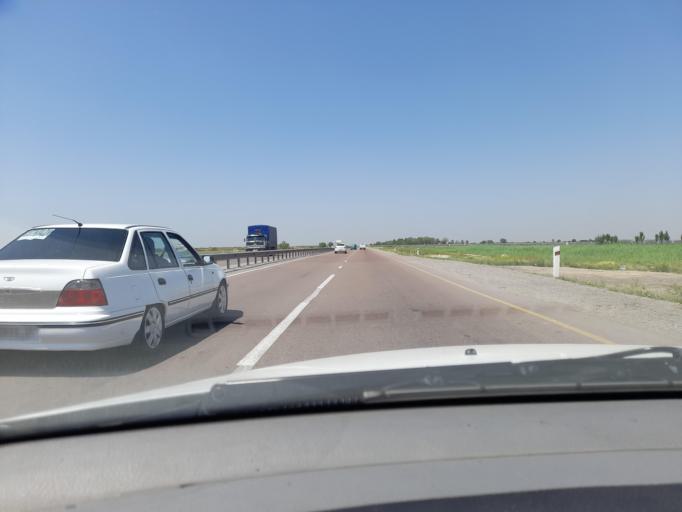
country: KZ
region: Ongtustik Qazaqstan
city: Myrzakent
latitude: 40.5099
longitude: 68.4973
